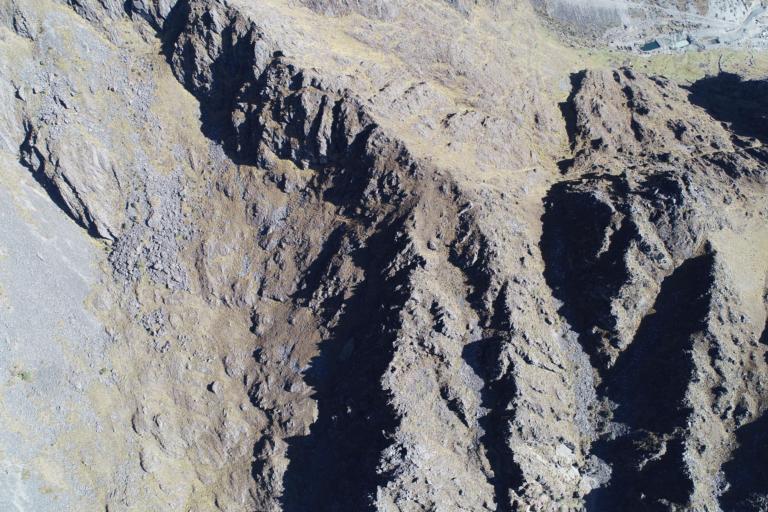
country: BO
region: La Paz
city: Sorata
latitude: -15.6566
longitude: -68.5327
